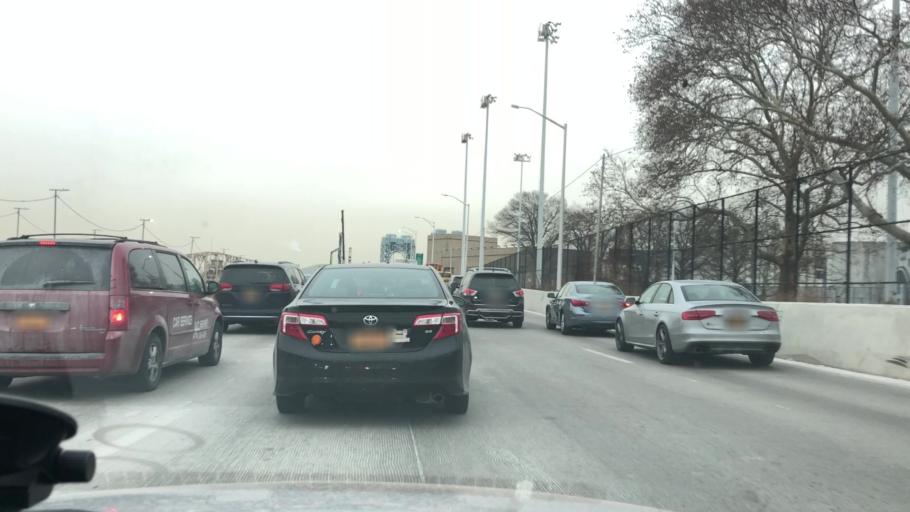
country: US
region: New York
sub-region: New York County
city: Manhattan
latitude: 40.8069
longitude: -73.9335
